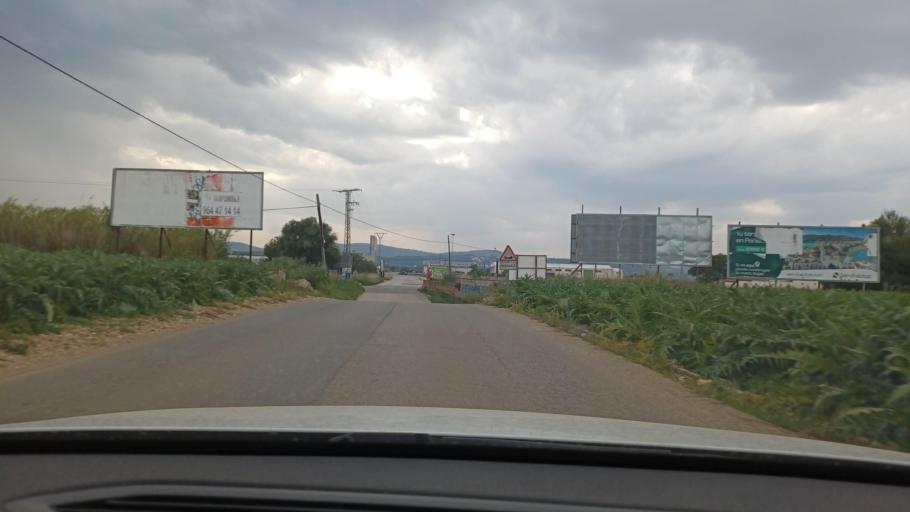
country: ES
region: Valencia
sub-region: Provincia de Castello
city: Benicarlo
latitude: 40.4086
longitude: 0.3954
